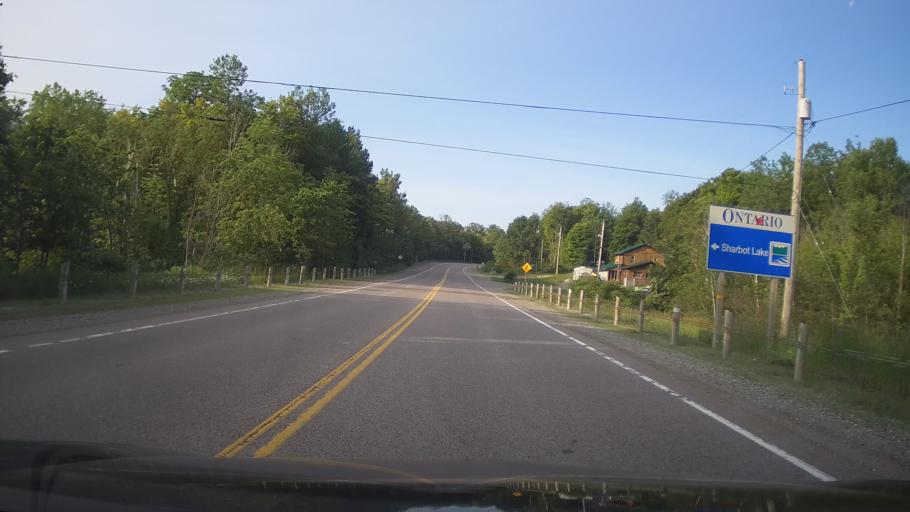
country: CA
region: Ontario
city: Perth
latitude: 44.7803
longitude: -76.7239
